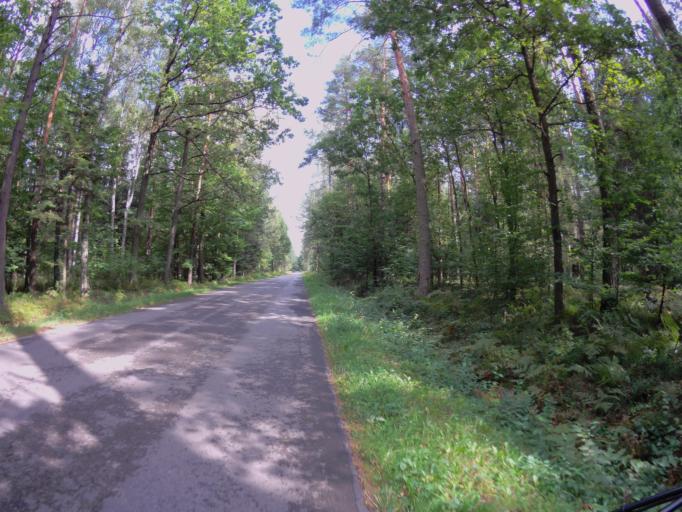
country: PL
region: Subcarpathian Voivodeship
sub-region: Powiat lezajski
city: Brzoza Krolewska
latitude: 50.2431
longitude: 22.3547
